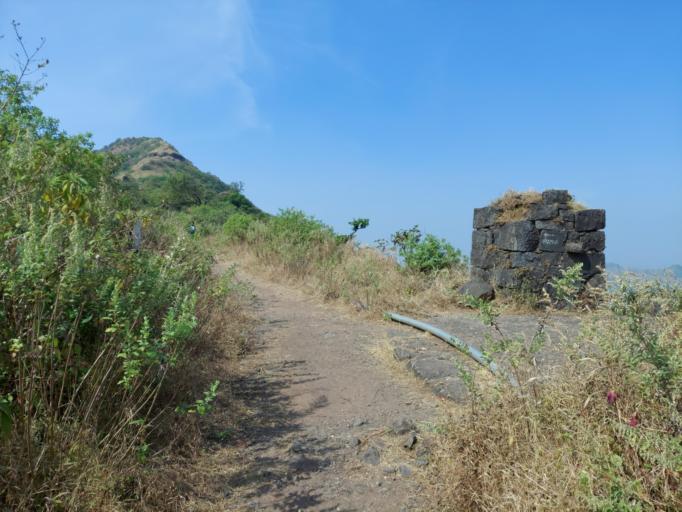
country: IN
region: Maharashtra
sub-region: Pune Division
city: Sasvad
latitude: 18.2804
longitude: 73.9781
